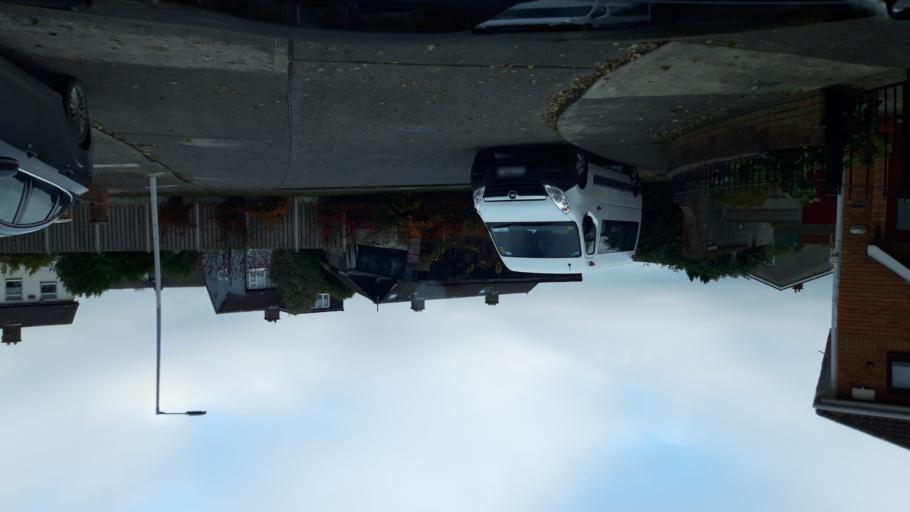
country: IE
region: Leinster
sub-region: Dublin City
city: Finglas
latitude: 53.3841
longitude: -6.2873
